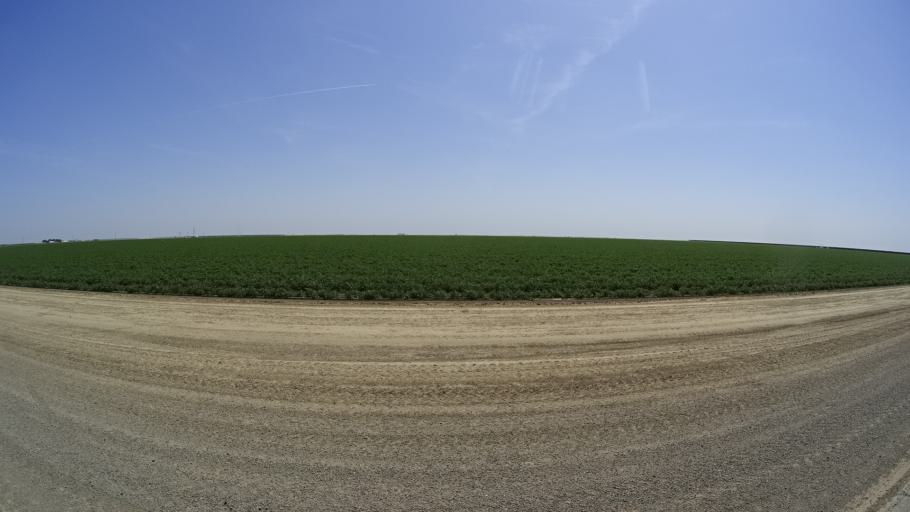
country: US
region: California
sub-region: Kings County
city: Kettleman City
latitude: 36.1187
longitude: -120.0037
